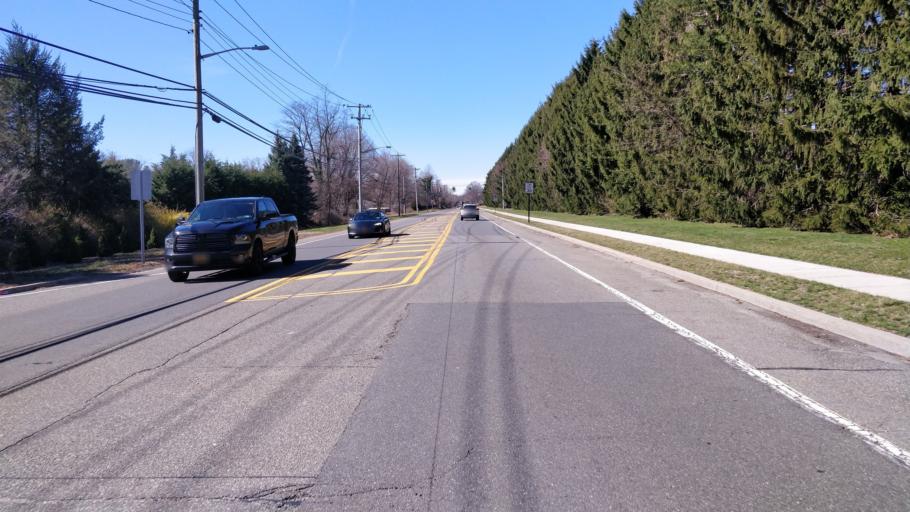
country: US
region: New York
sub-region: Suffolk County
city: Huntington Station
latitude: 40.8550
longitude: -73.3931
